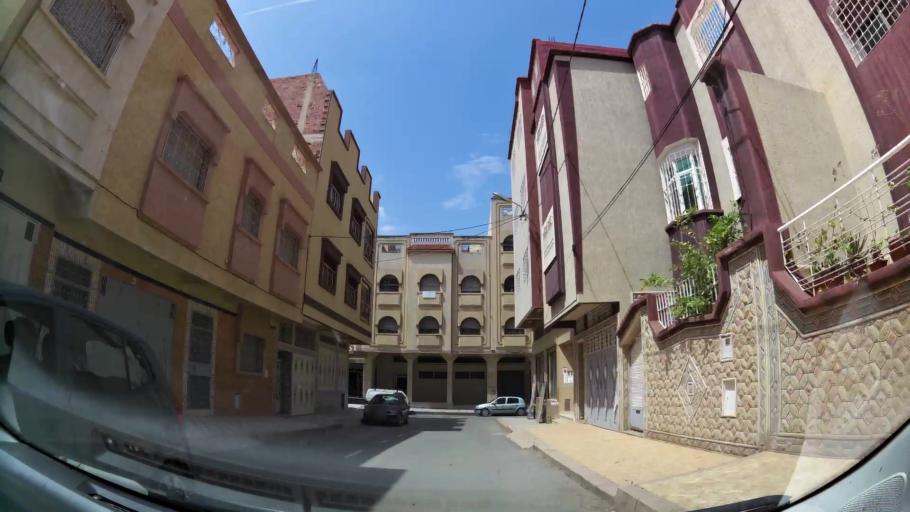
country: MA
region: Oriental
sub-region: Oujda-Angad
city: Oujda
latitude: 34.6840
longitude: -1.8812
